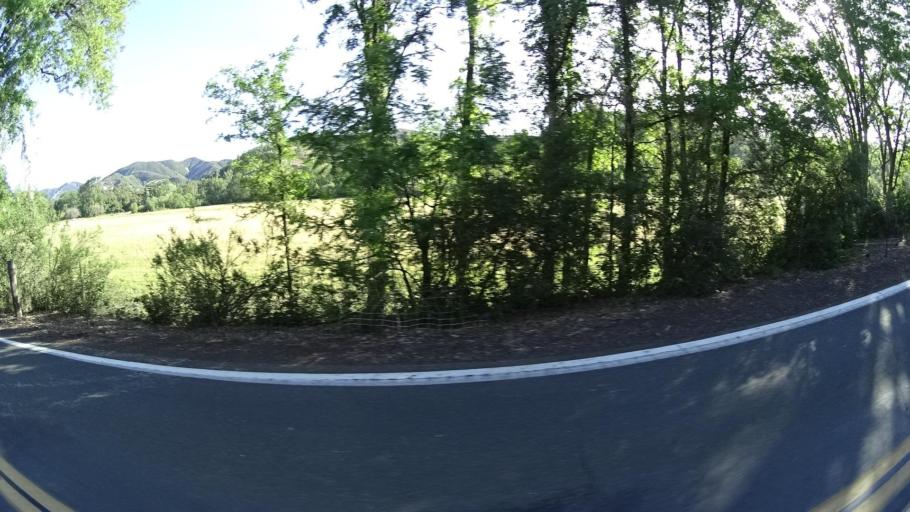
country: US
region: California
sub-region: Lake County
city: North Lakeport
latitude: 39.1138
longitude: -122.9830
